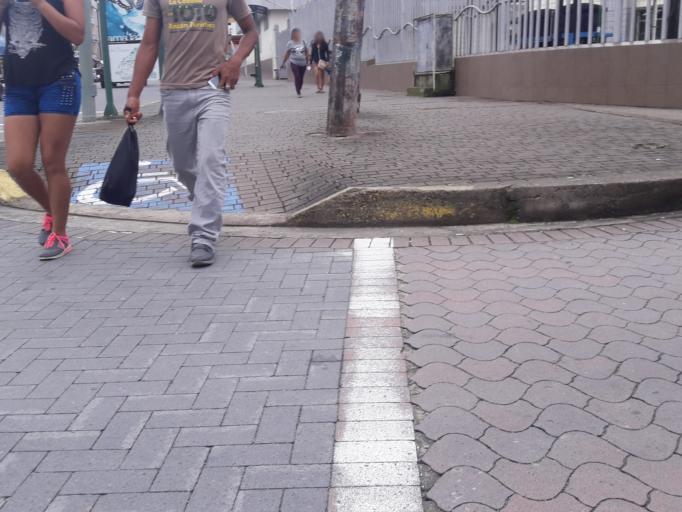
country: EC
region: Napo
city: Tena
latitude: -1.0034
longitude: -77.8113
